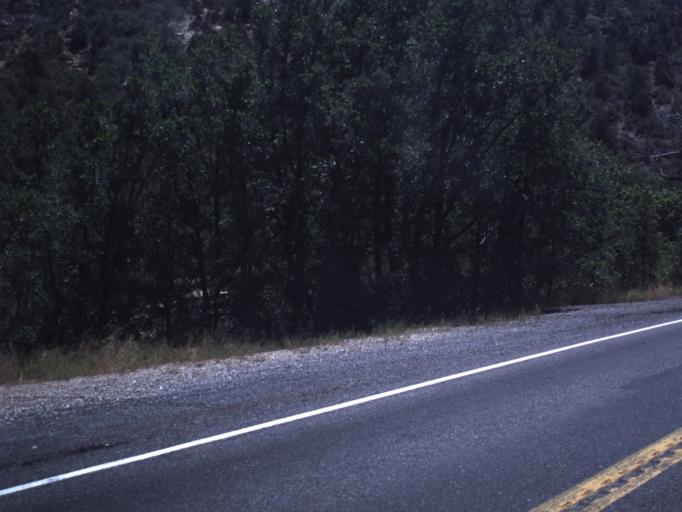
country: US
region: Utah
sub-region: Kane County
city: Kanab
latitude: 37.3663
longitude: -112.5926
